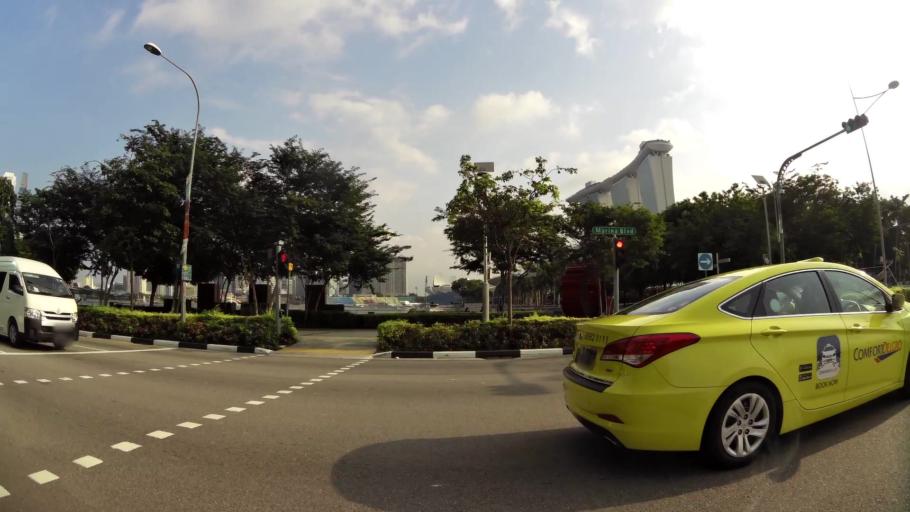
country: SG
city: Singapore
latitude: 1.2798
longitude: 103.8557
